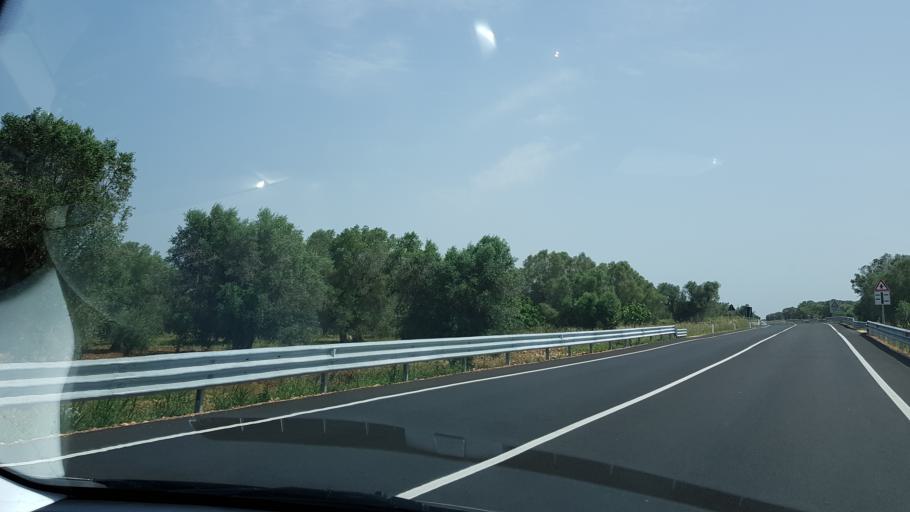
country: IT
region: Apulia
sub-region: Provincia di Brindisi
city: San Pancrazio Salentino
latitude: 40.4669
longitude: 17.8383
